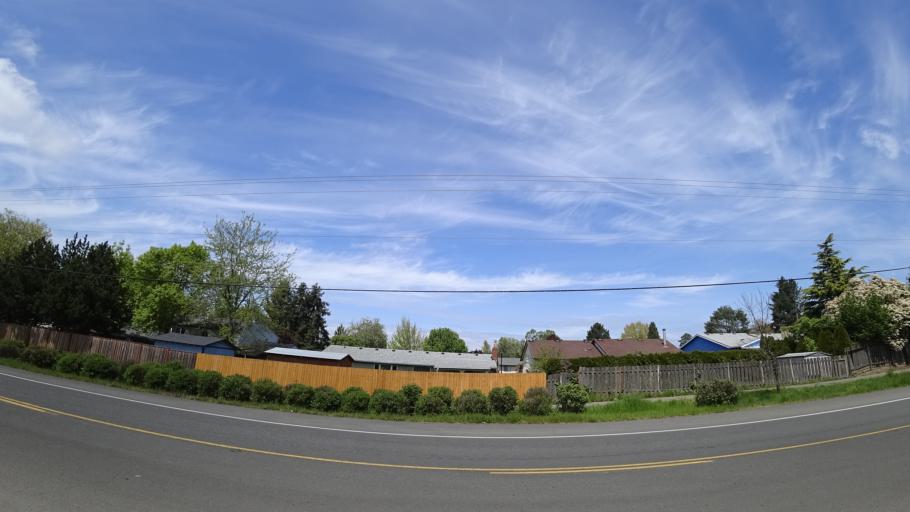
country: US
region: Oregon
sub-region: Washington County
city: Aloha
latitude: 45.4688
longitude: -122.8865
